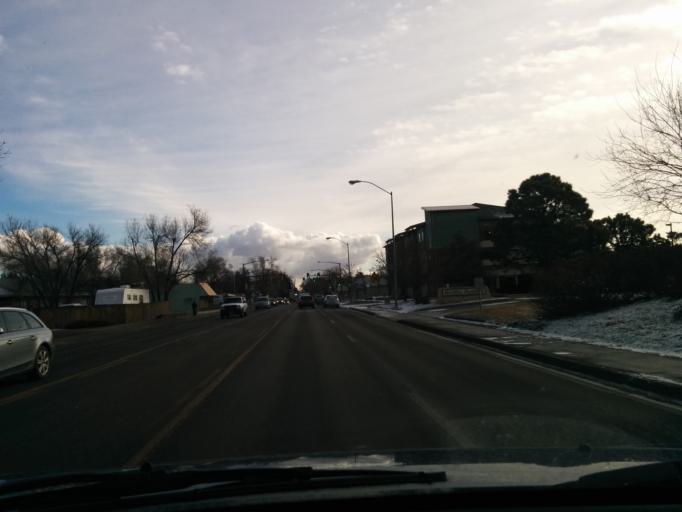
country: US
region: Colorado
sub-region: Larimer County
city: Fort Collins
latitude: 40.5671
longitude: -105.0810
